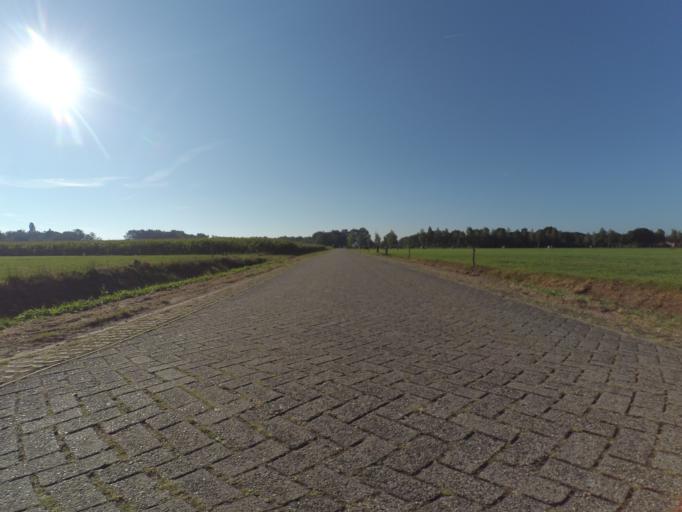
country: NL
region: Gelderland
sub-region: Gemeente Barneveld
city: Zwartebroek
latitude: 52.2155
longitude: 5.5409
